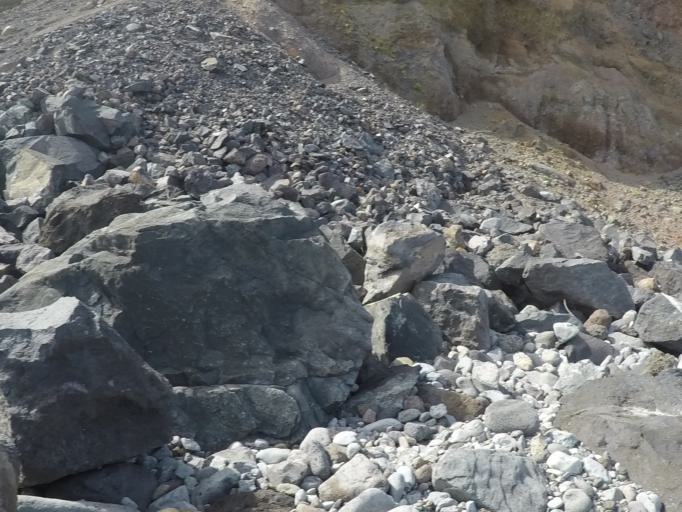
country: PT
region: Madeira
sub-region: Sao Vicente
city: Sao Vicente
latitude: 32.8099
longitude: -16.9696
